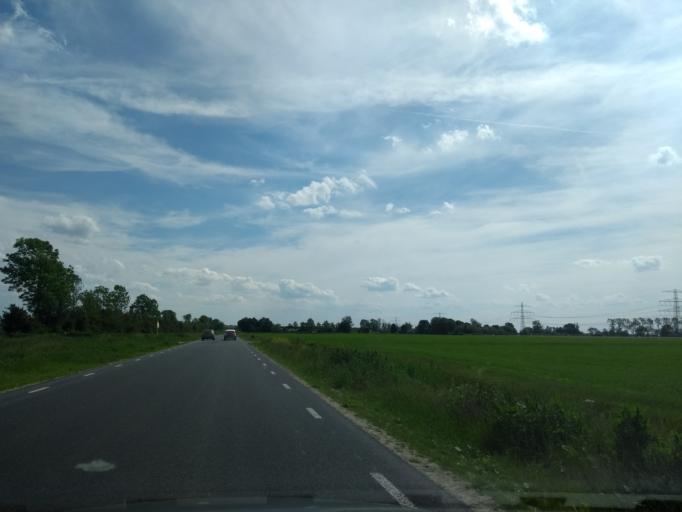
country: NL
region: Groningen
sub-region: Gemeente Zuidhorn
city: Aduard
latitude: 53.2515
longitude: 6.4804
